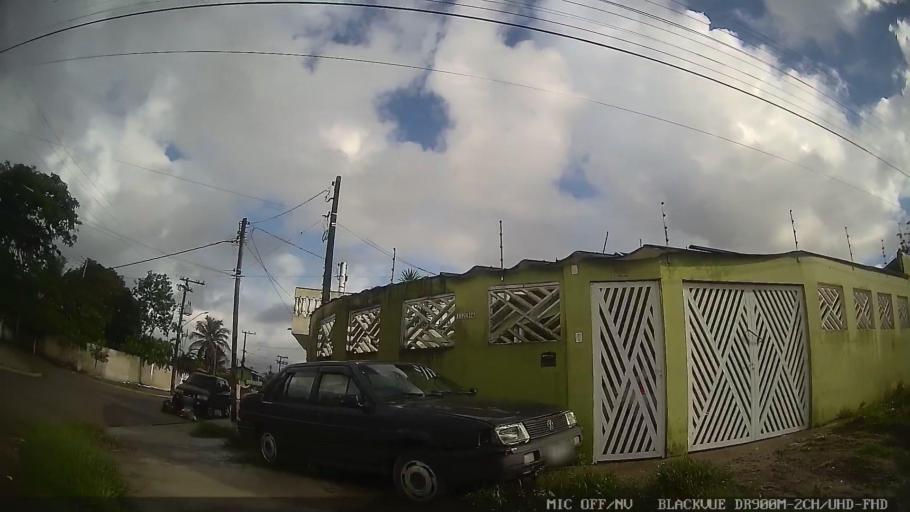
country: BR
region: Sao Paulo
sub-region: Itanhaem
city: Itanhaem
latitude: -24.1793
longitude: -46.8535
